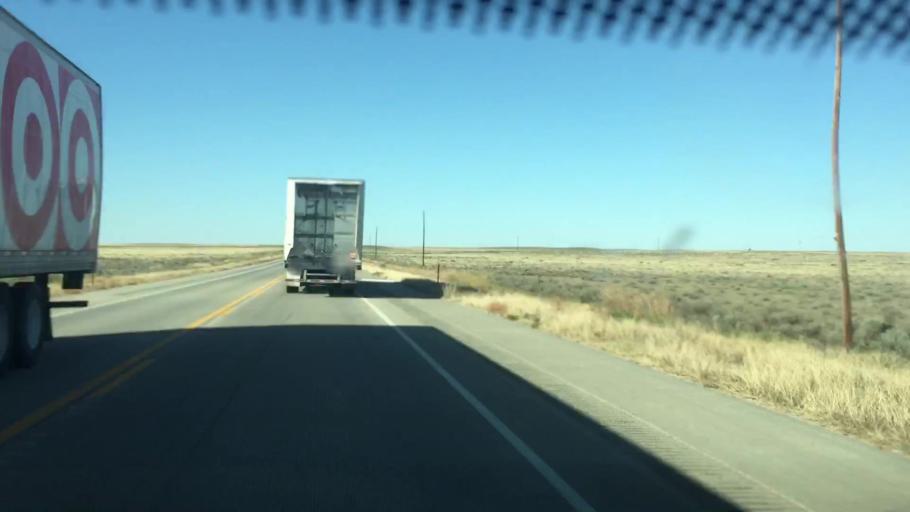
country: US
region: Colorado
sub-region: Kiowa County
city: Eads
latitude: 38.6174
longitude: -102.7859
